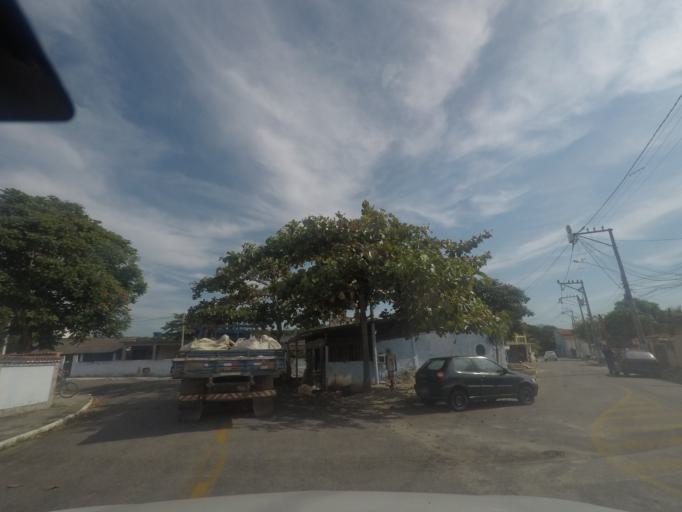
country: BR
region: Rio de Janeiro
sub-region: Marica
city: Marica
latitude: -22.9548
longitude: -42.8104
